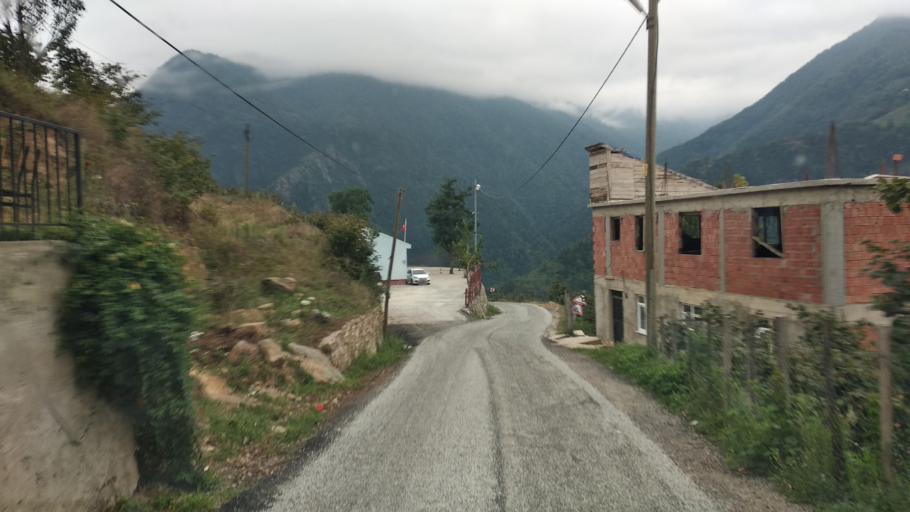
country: TR
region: Giresun
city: Dogankent
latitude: 40.7440
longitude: 38.9913
